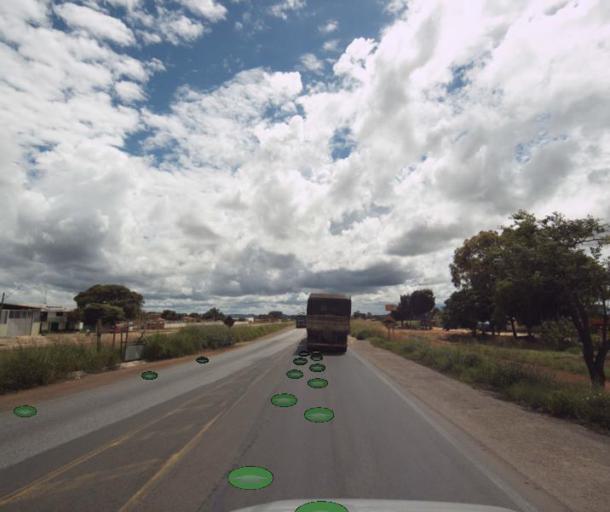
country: BR
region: Goias
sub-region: Uruacu
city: Uruacu
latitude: -14.3129
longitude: -49.1496
